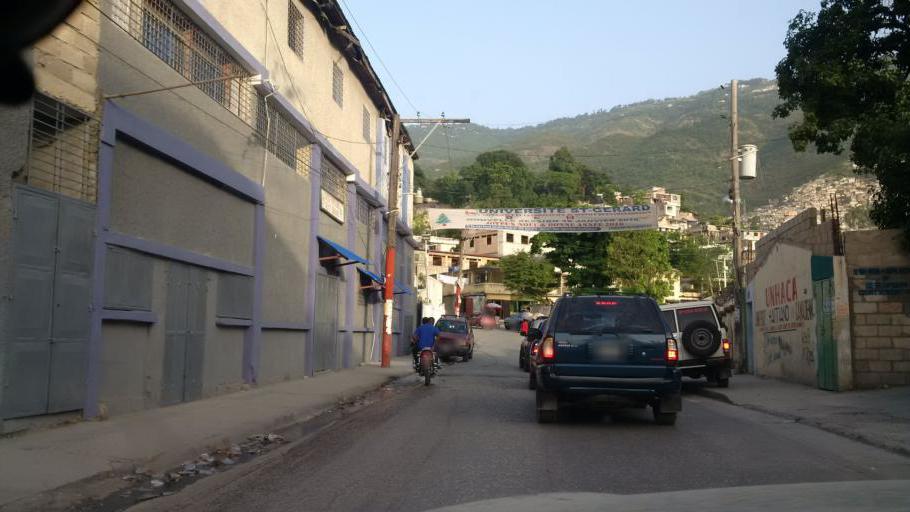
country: HT
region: Ouest
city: Port-au-Prince
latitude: 18.5288
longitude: -72.3400
